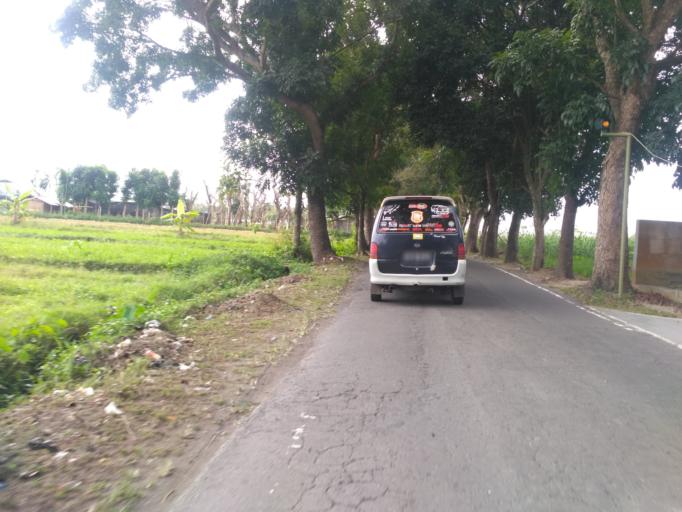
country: ID
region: Daerah Istimewa Yogyakarta
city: Melati
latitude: -7.7345
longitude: 110.3534
